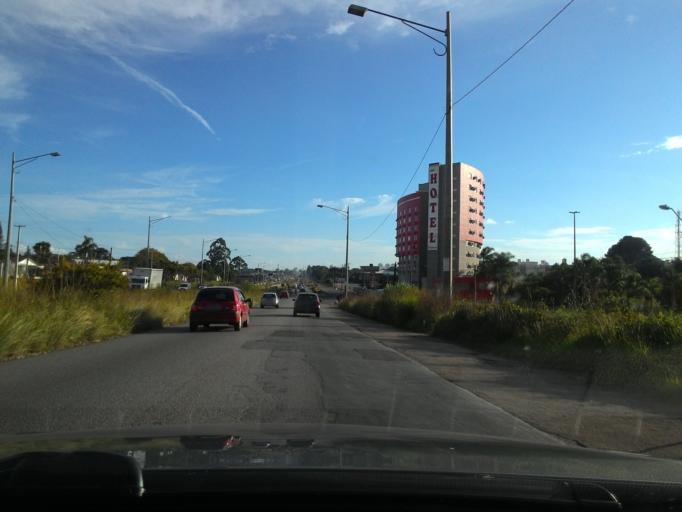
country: BR
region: Parana
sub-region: Pinhais
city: Pinhais
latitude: -25.4032
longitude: -49.2174
